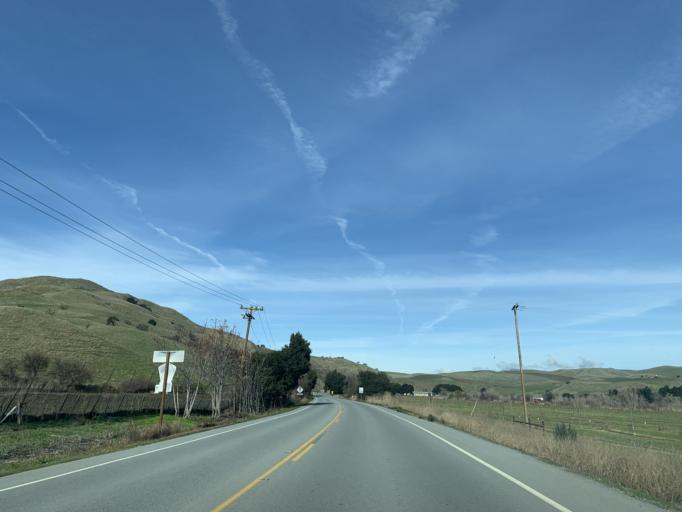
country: US
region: California
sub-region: San Benito County
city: Ridgemark
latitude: 36.7300
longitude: -121.2790
